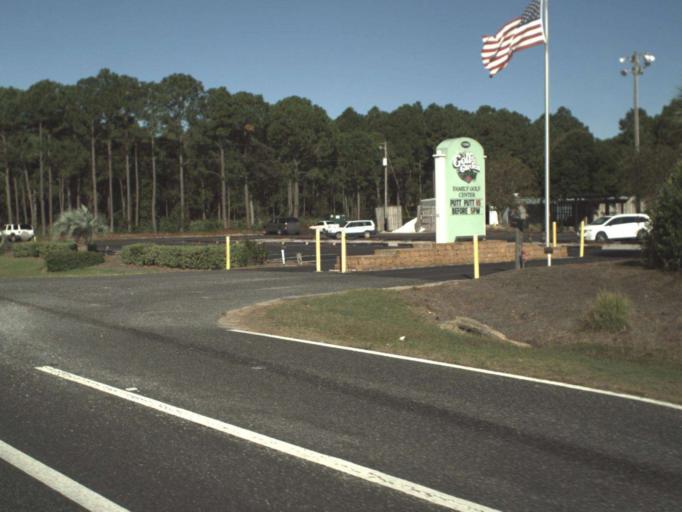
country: US
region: Florida
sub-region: Walton County
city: Miramar Beach
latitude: 30.3853
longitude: -86.3879
